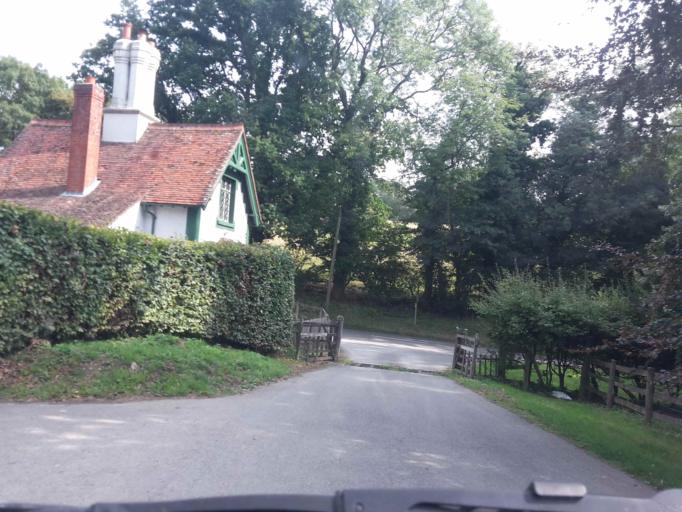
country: GB
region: England
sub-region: Oxfordshire
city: Rotherfield Peppard
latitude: 51.5452
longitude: -0.9514
